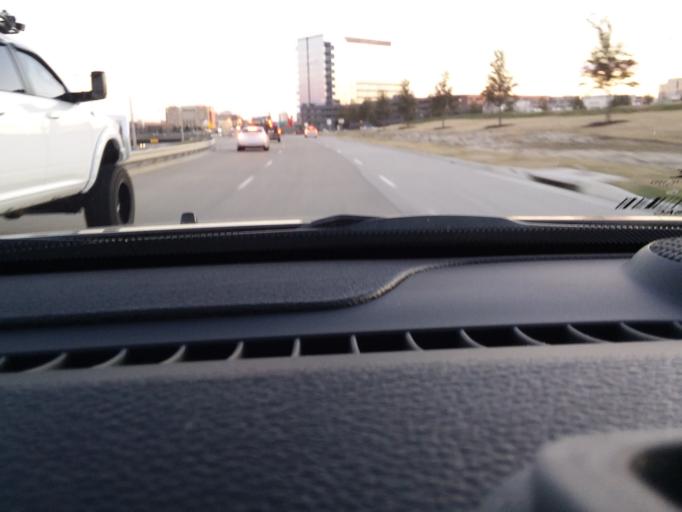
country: US
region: Texas
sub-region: Collin County
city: Frisco
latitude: 33.1083
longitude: -96.8240
